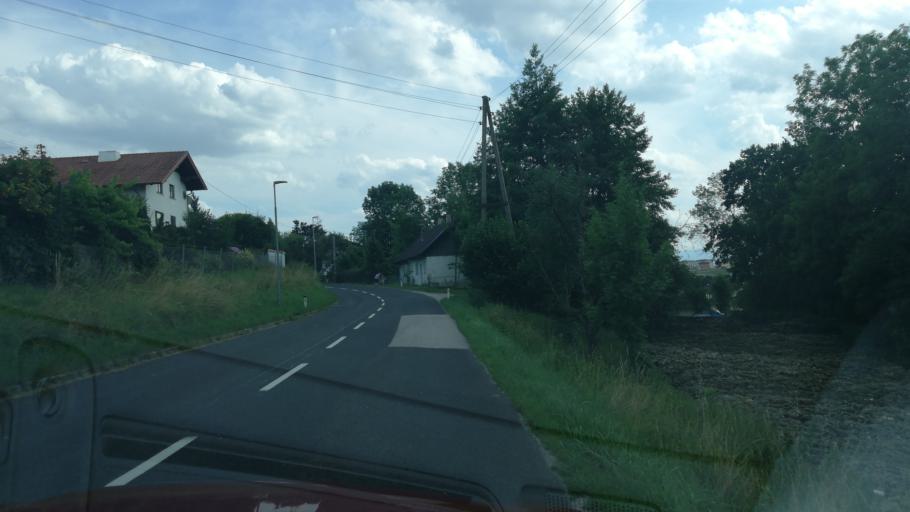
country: AT
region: Upper Austria
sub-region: Wels-Land
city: Lambach
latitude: 48.0990
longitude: 13.8626
